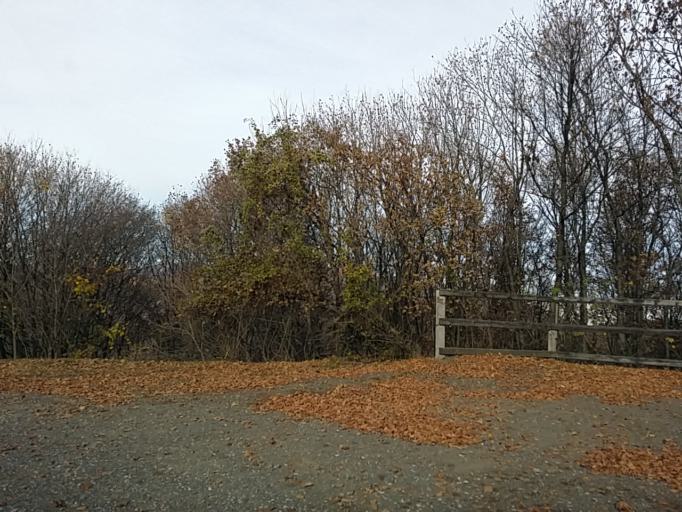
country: HU
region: Heves
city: Paradsasvar
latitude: 47.8725
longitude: 19.9847
